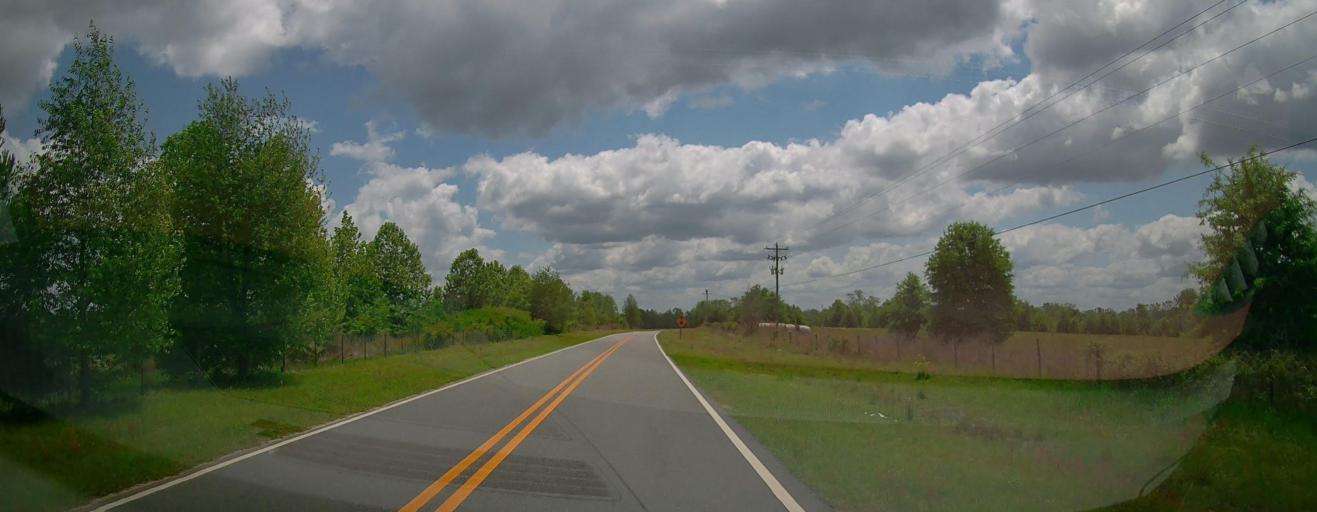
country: US
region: Georgia
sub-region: Laurens County
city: Dublin
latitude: 32.5979
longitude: -82.9323
